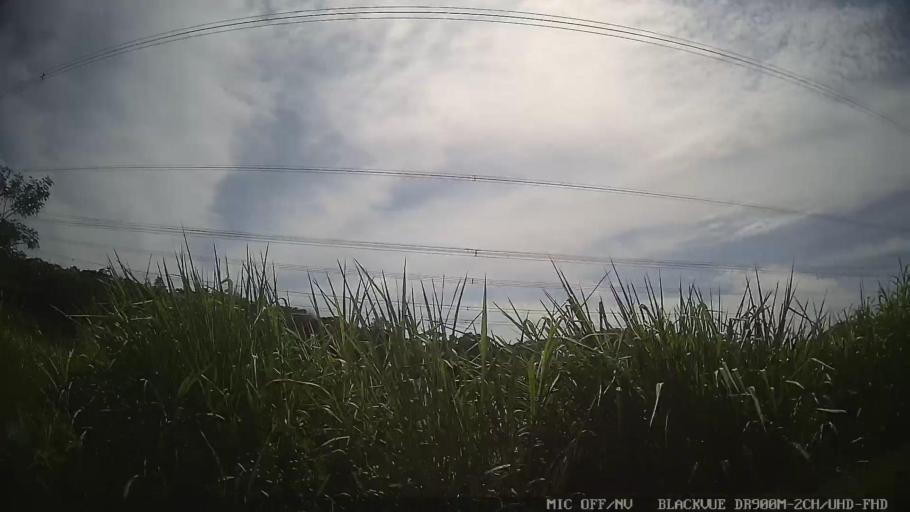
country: BR
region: Sao Paulo
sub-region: Suzano
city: Suzano
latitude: -23.4892
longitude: -46.2642
